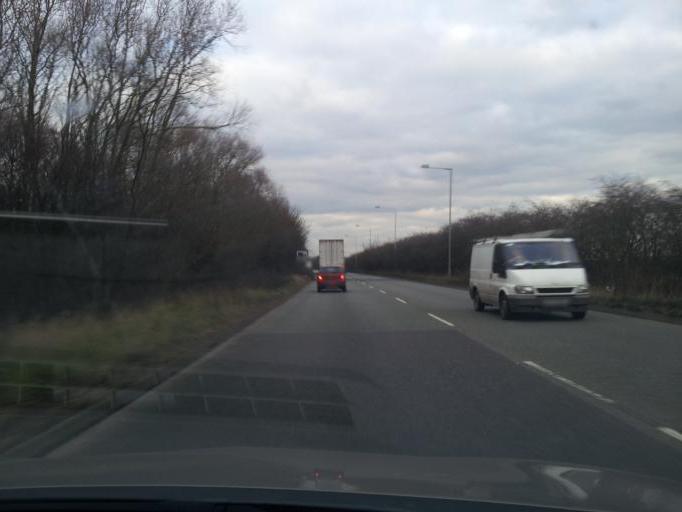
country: GB
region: England
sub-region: Nottinghamshire
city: West Bridgford
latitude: 52.9173
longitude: -1.0998
